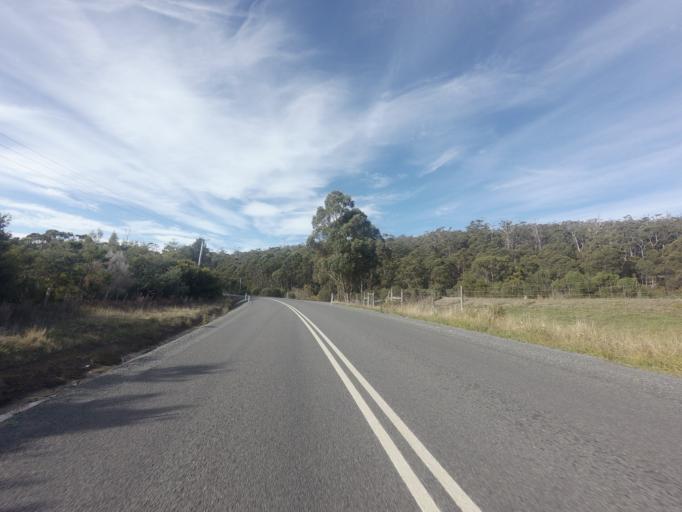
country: AU
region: Tasmania
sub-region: Clarence
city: Sandford
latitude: -43.0639
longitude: 147.8408
